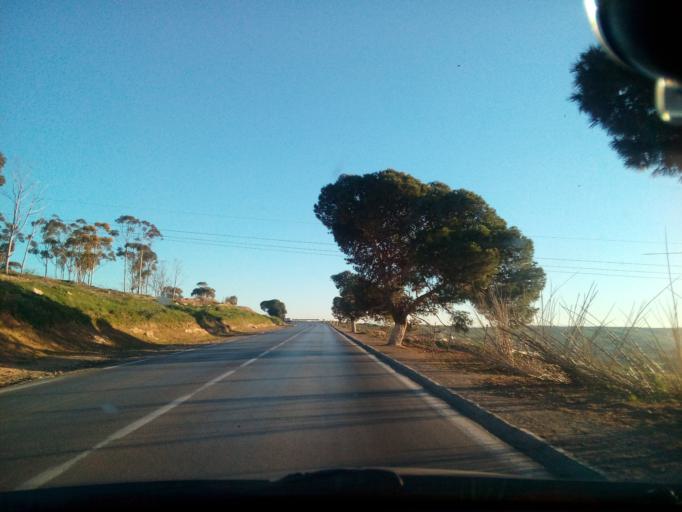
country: DZ
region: Mostaganem
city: Mostaganem
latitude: 35.7634
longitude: 0.2055
